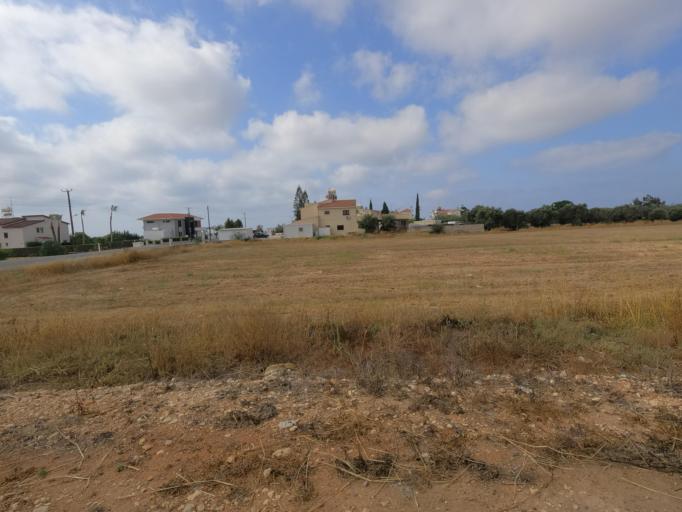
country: CY
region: Ammochostos
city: Ayia Napa
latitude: 35.0030
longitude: 34.0046
